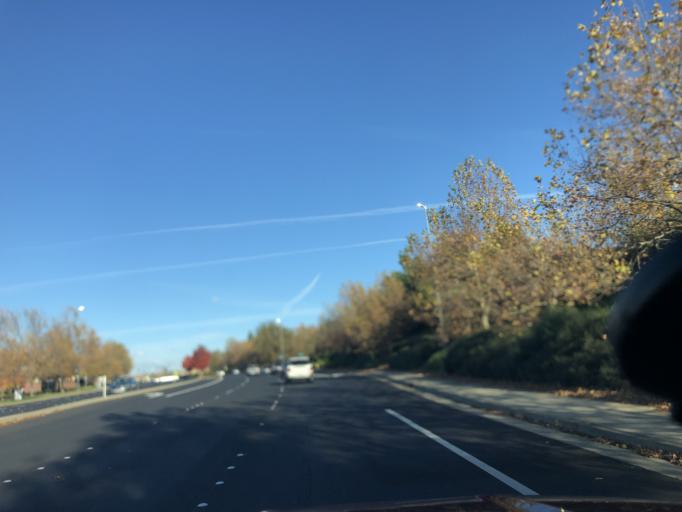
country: US
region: California
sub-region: Placer County
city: Roseville
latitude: 38.7760
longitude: -121.2910
